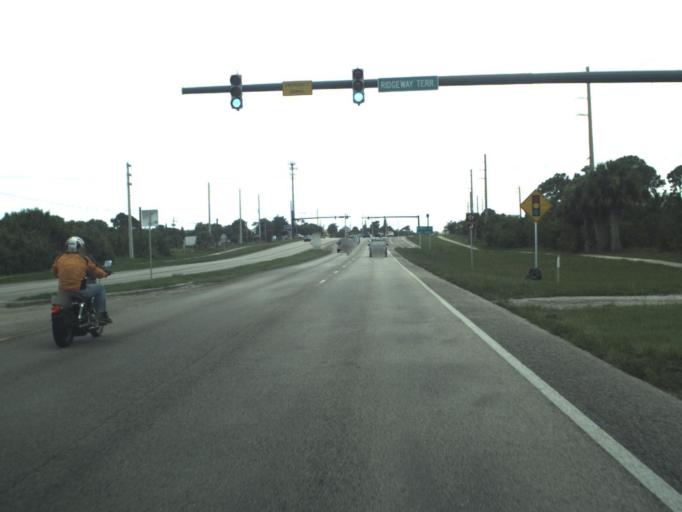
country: US
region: Florida
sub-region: Martin County
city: Hobe Sound
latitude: 27.1009
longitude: -80.1615
